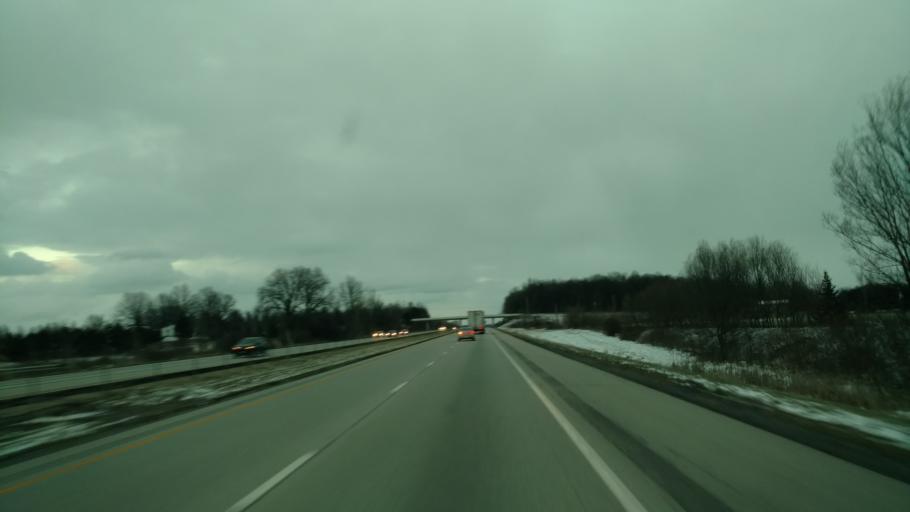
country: US
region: Ohio
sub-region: Medina County
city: Seville
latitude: 41.0319
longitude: -81.8147
